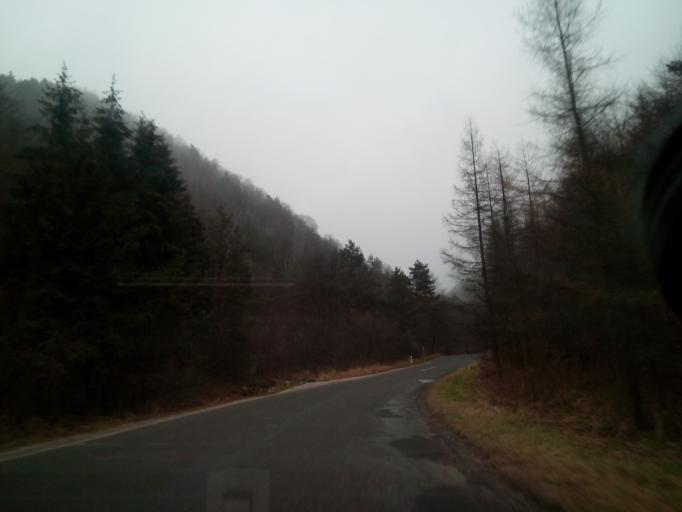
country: SK
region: Kosicky
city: Krompachy
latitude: 48.9455
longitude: 20.9480
